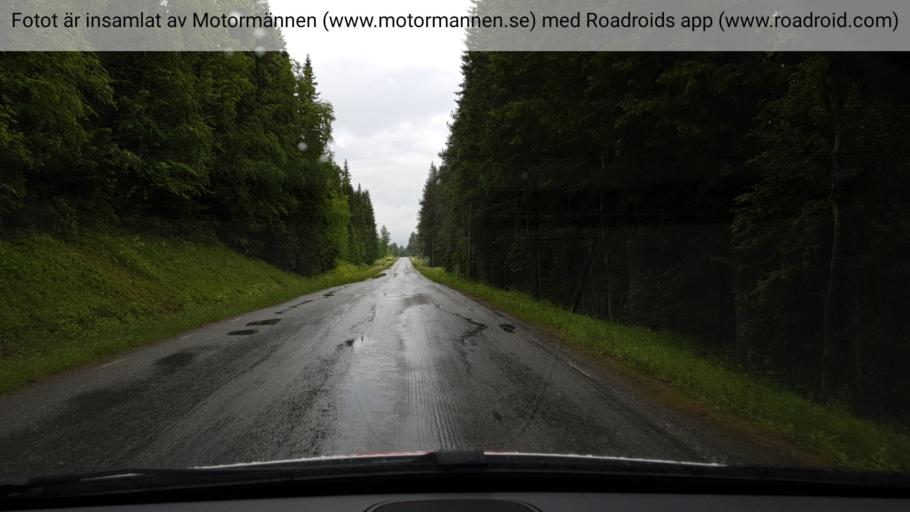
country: SE
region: Jaemtland
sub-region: Stroemsunds Kommun
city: Stroemsund
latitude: 64.2604
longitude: 15.7991
